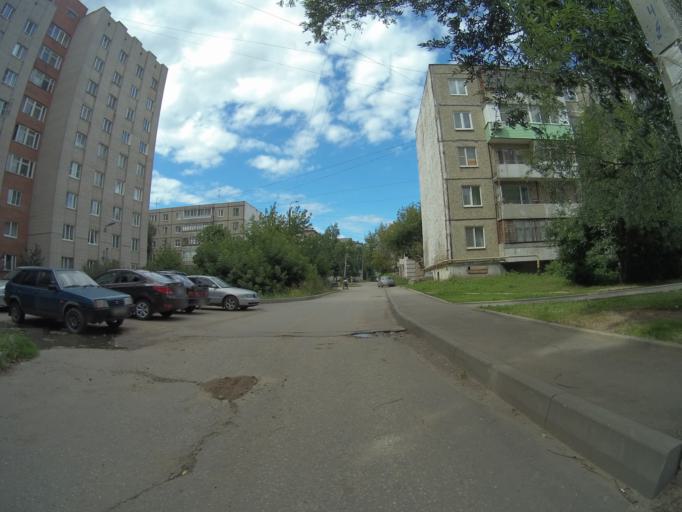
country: RU
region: Vladimir
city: Vladimir
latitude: 56.1182
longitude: 40.3756
